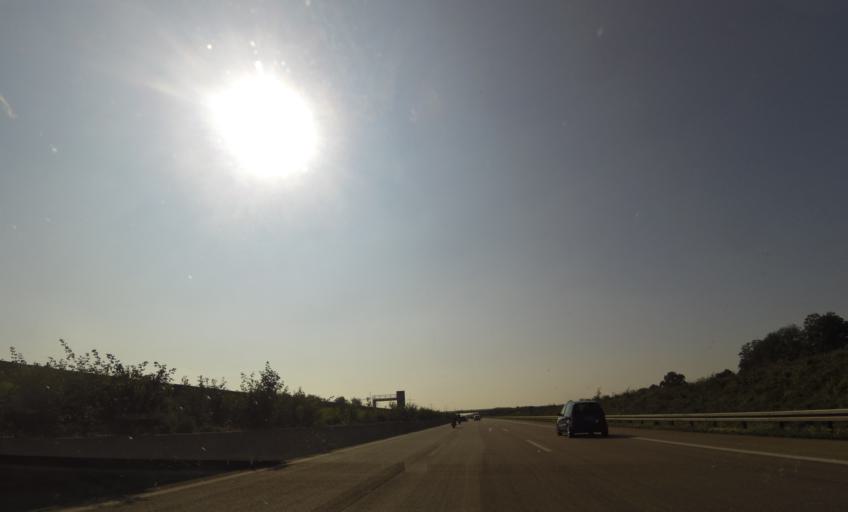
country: DE
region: Baden-Wuerttemberg
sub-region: Karlsruhe Region
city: Ottenhofen
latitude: 48.7440
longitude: 8.1205
